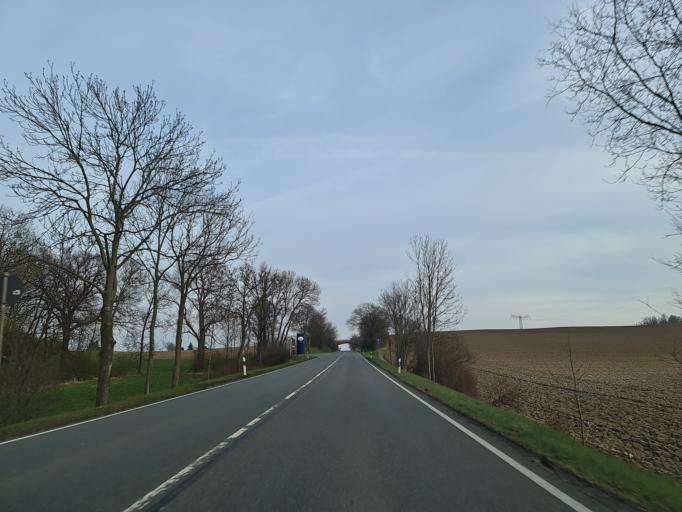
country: DE
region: Saxony
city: Plauen
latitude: 50.4643
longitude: 12.1529
